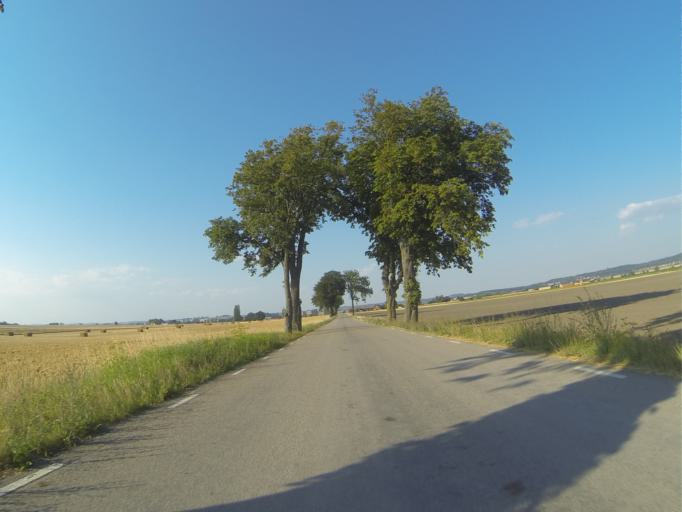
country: SE
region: Skane
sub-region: Lunds Kommun
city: Genarp
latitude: 55.6037
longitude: 13.3659
